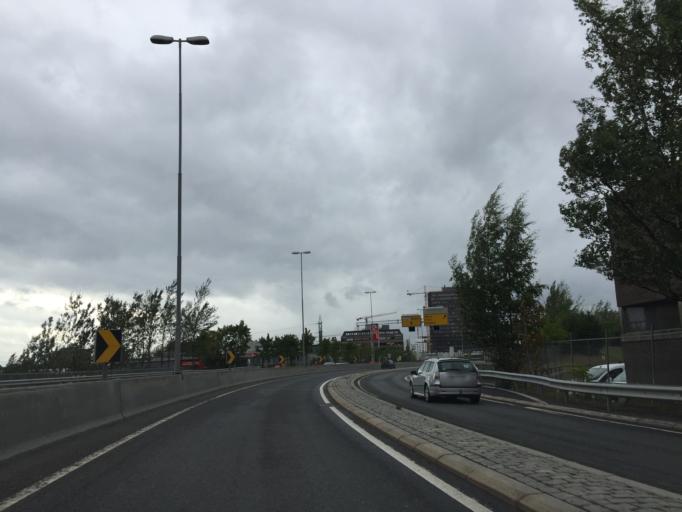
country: NO
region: Oslo
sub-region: Oslo
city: Oslo
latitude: 59.9278
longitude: 10.8133
